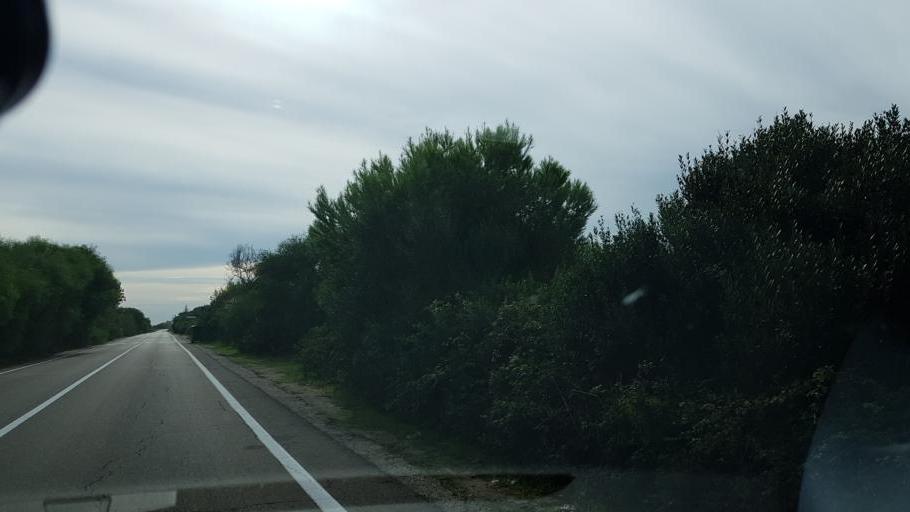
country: IT
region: Apulia
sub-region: Provincia di Lecce
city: Melendugno
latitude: 40.3106
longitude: 18.3911
